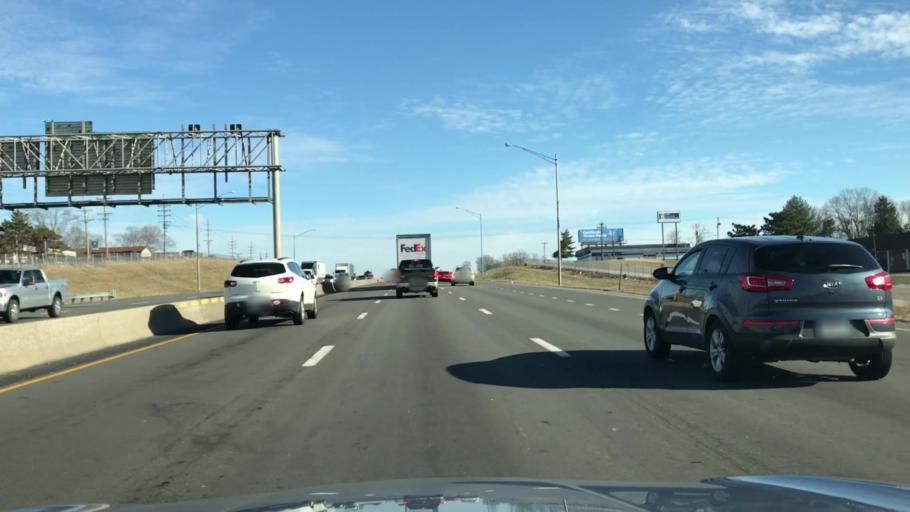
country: US
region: Missouri
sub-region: Saint Louis County
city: Calverton Park
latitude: 38.7723
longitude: -90.3043
